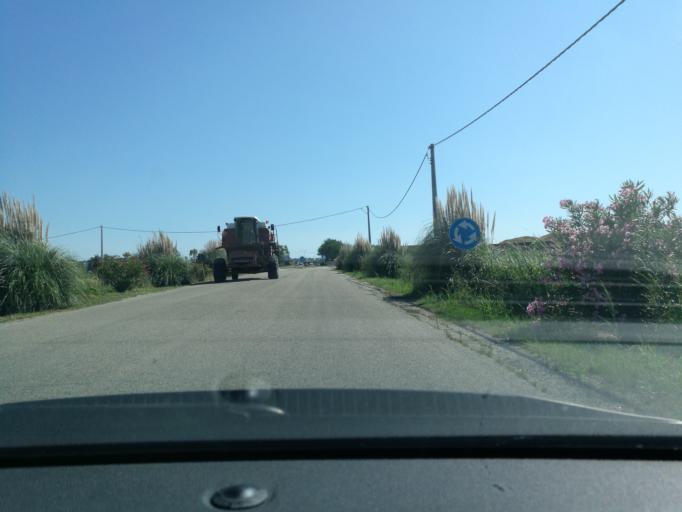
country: IT
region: Abruzzo
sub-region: Provincia di Chieti
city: Vasto
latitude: 42.1706
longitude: 14.6961
